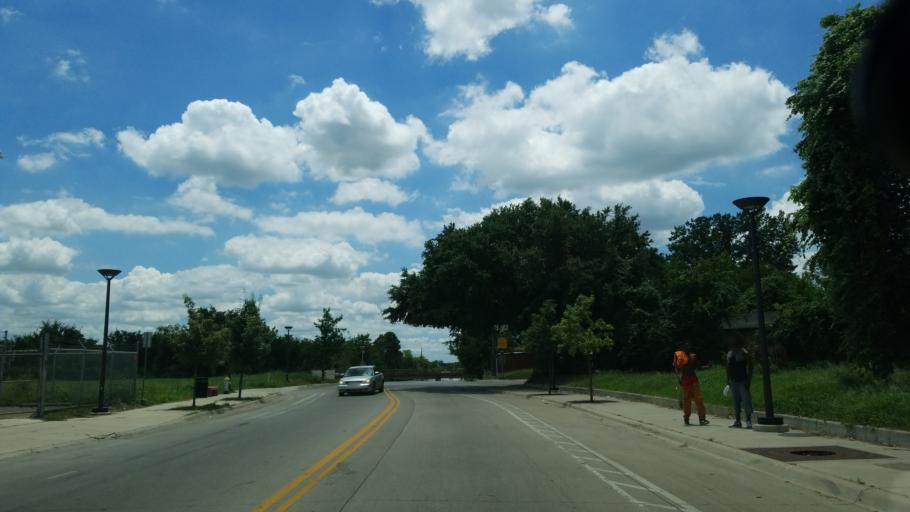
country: US
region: Texas
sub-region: Dallas County
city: Dallas
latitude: 32.7454
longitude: -96.7534
